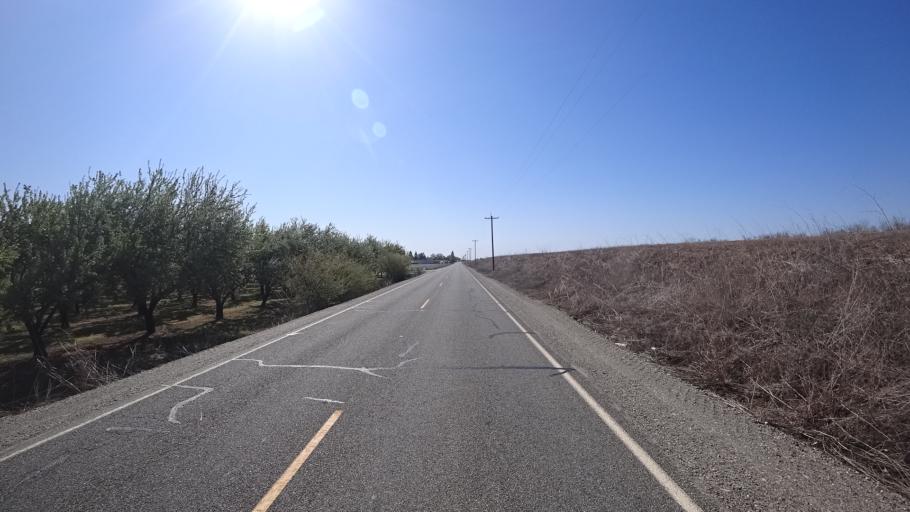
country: US
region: California
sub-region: Glenn County
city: Hamilton City
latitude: 39.7514
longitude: -122.0228
